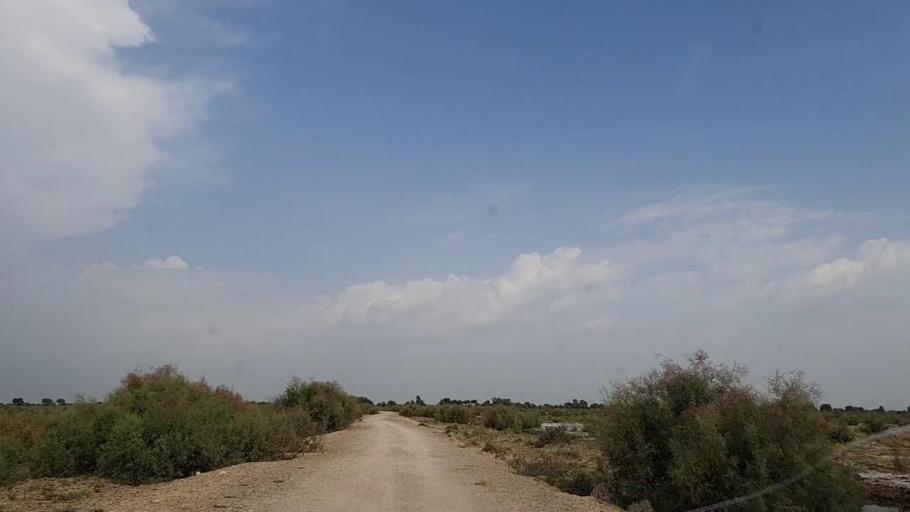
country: PK
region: Sindh
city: Khanpur
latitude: 27.8196
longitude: 69.5289
